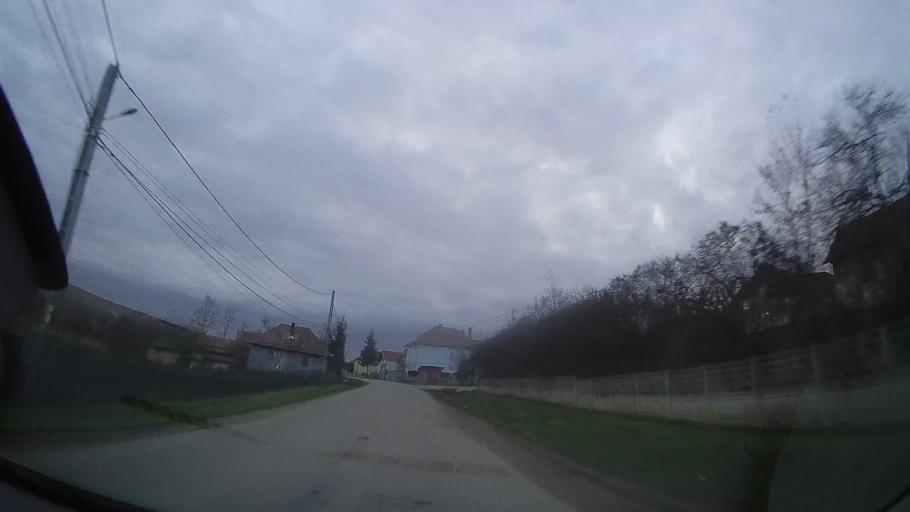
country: RO
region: Cluj
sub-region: Comuna Caianu
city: Vaida-Camaras
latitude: 46.8272
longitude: 23.9448
